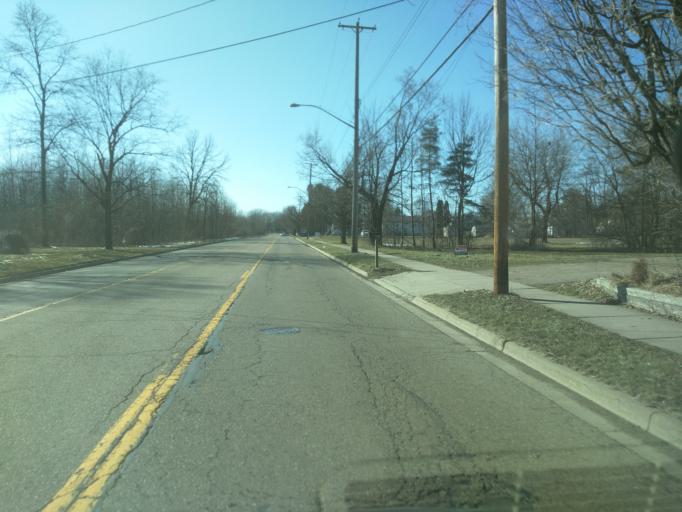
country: US
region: Michigan
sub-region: Eaton County
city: Dimondale
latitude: 42.6693
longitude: -84.5959
